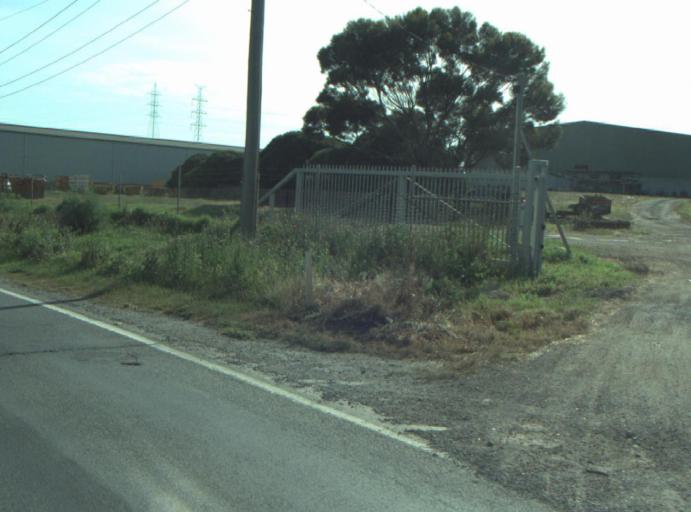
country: AU
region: Victoria
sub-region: Greater Geelong
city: Leopold
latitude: -38.1615
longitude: 144.4292
